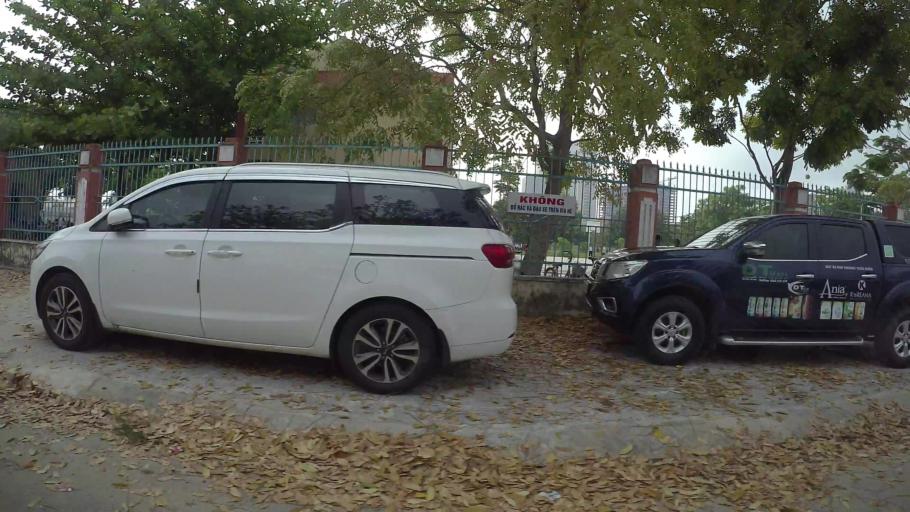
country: VN
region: Da Nang
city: Son Tra
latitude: 16.0804
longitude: 108.2415
